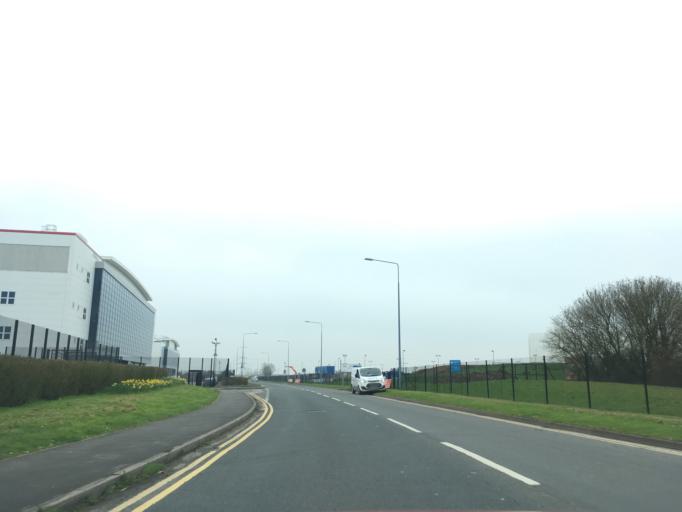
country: GB
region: Wales
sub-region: Newport
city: Marshfield
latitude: 51.5559
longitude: -3.0401
